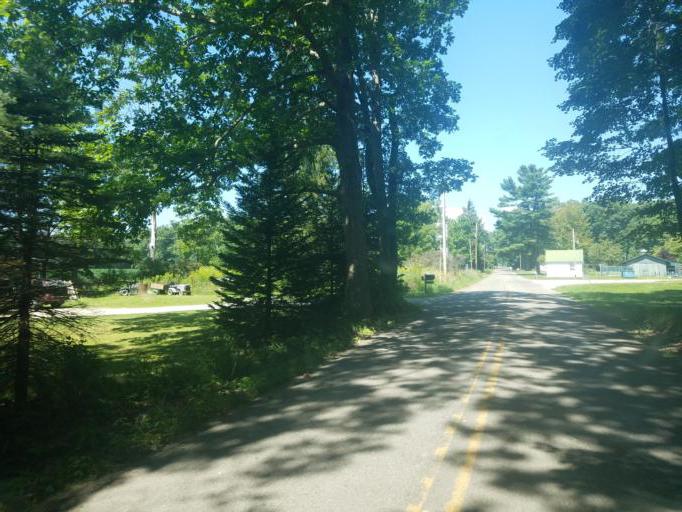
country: US
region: Pennsylvania
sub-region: Clarion County
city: Knox
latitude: 41.1906
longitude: -79.4891
